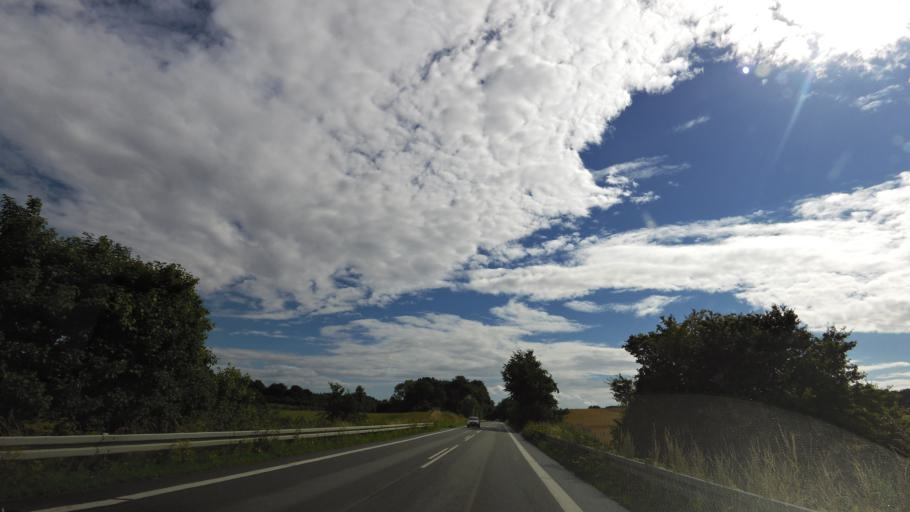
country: DK
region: South Denmark
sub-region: Assens Kommune
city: Vissenbjerg
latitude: 55.4217
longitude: 10.1785
